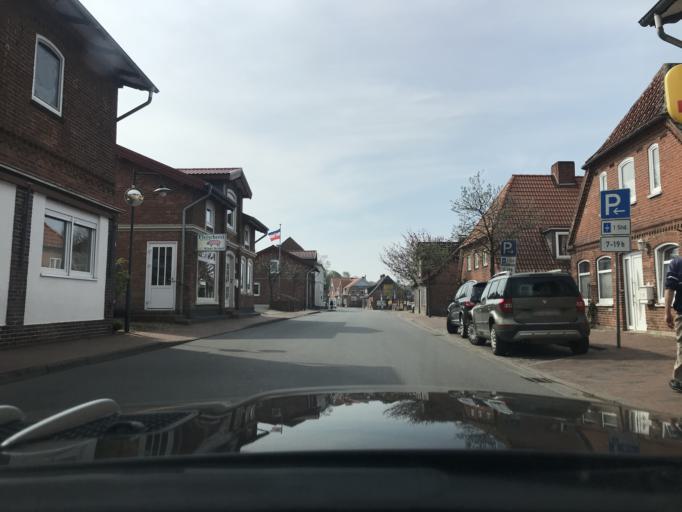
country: DE
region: Schleswig-Holstein
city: Grube
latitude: 54.2319
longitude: 11.0361
